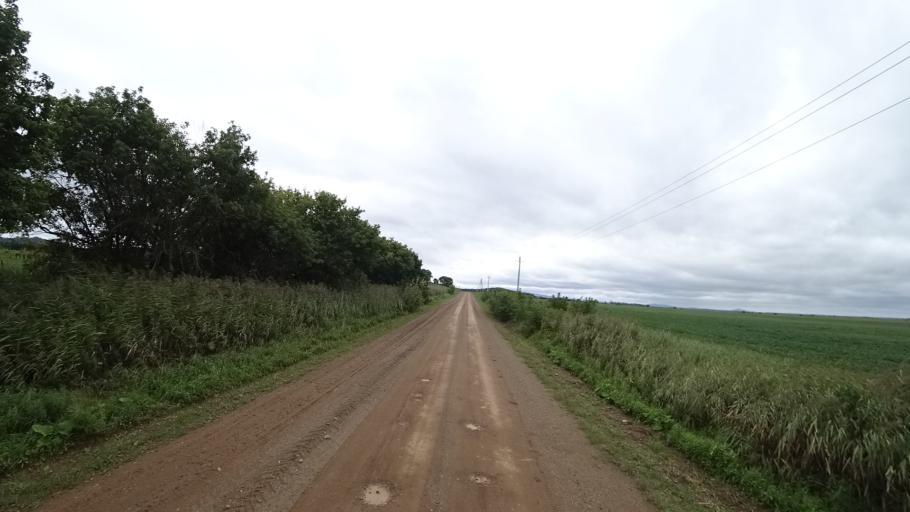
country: RU
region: Primorskiy
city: Chernigovka
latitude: 44.4864
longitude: 132.5733
